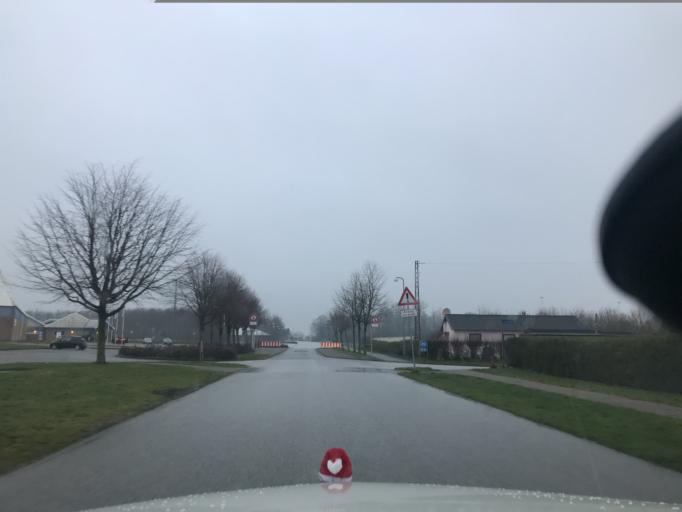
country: DK
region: South Denmark
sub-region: Aabenraa Kommune
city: Krusa
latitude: 54.8490
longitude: 9.4103
